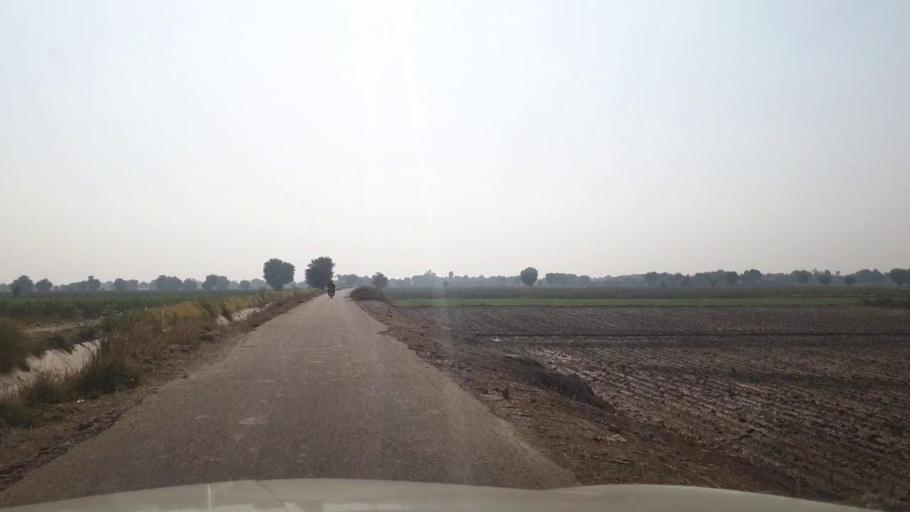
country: PK
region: Sindh
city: Bhan
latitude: 26.5239
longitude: 67.7795
